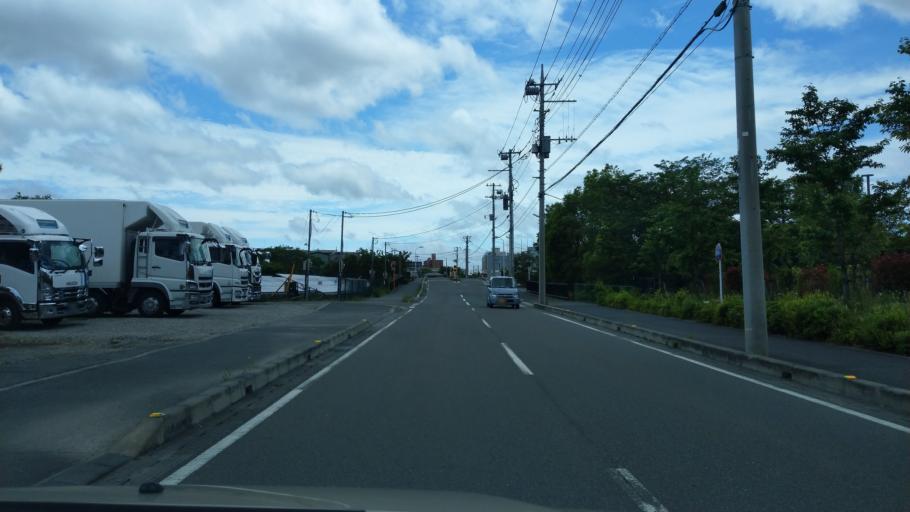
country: JP
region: Saitama
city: Shiki
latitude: 35.8446
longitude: 139.6193
